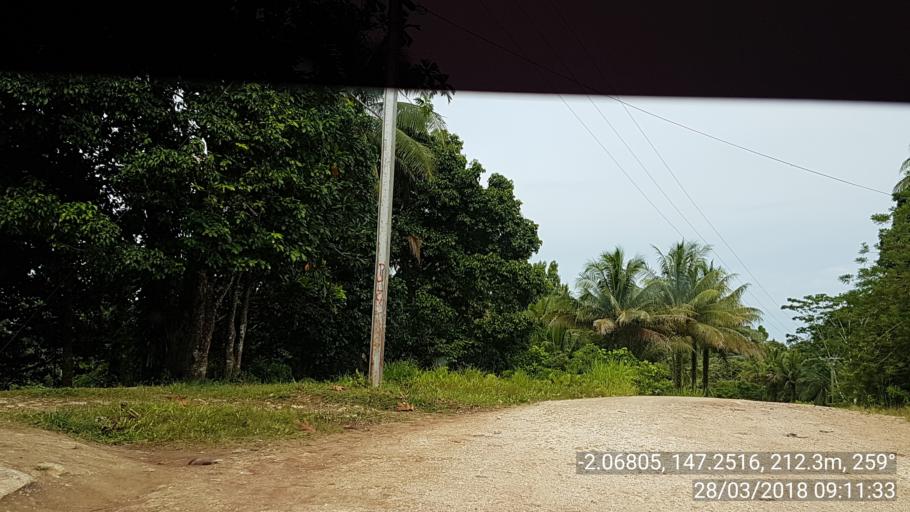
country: PG
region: Manus
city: Lorengau
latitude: -2.0680
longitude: 147.2516
